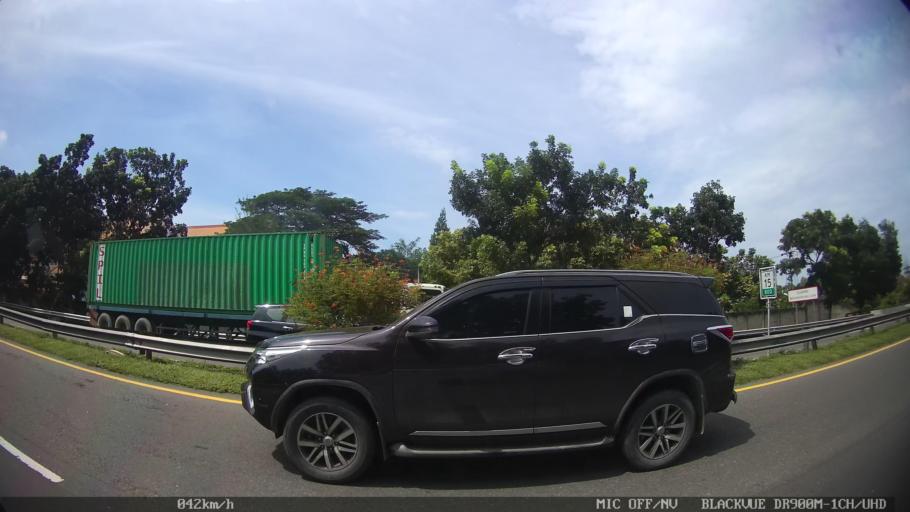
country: ID
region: North Sumatra
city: Medan
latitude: 3.6399
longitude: 98.6999
